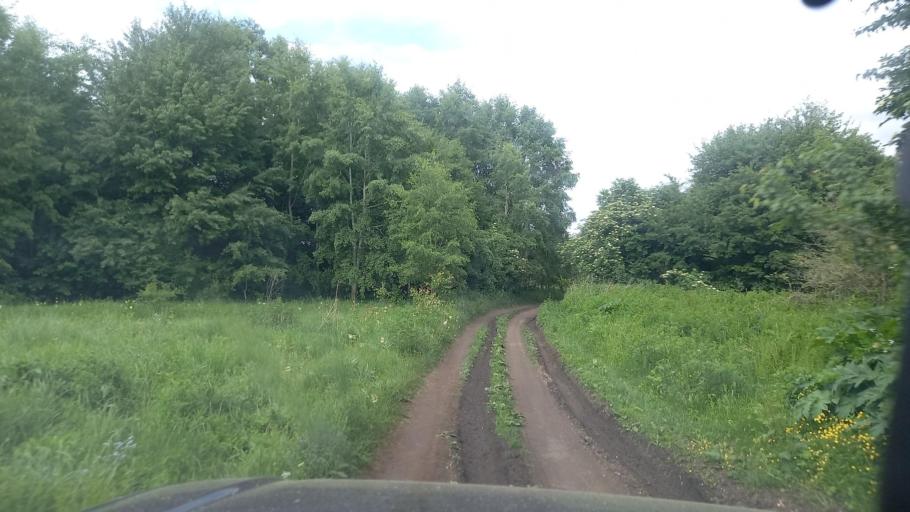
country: RU
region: Karachayevo-Cherkesiya
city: Pregradnaya
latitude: 44.0360
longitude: 41.3171
